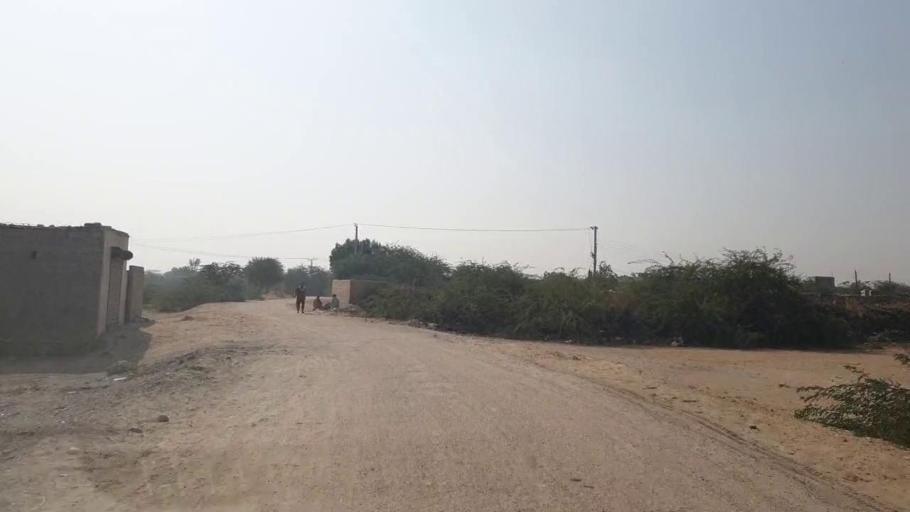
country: PK
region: Sindh
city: Kotri
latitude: 25.3403
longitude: 68.2827
